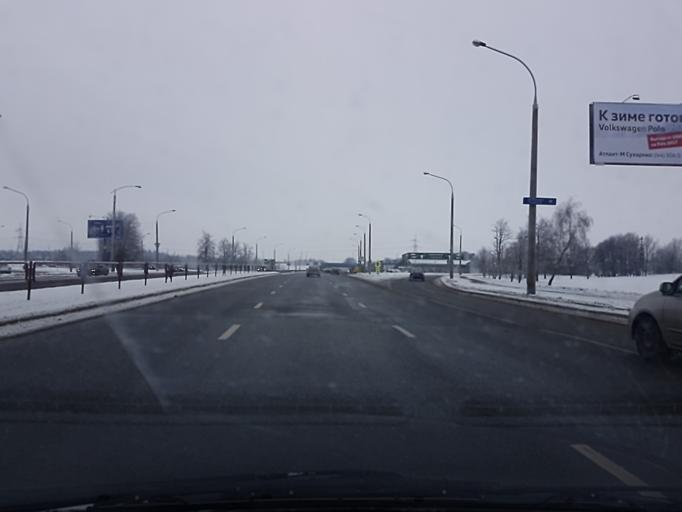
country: BY
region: Minsk
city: Shchomyslitsa
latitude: 53.8462
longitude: 27.4725
